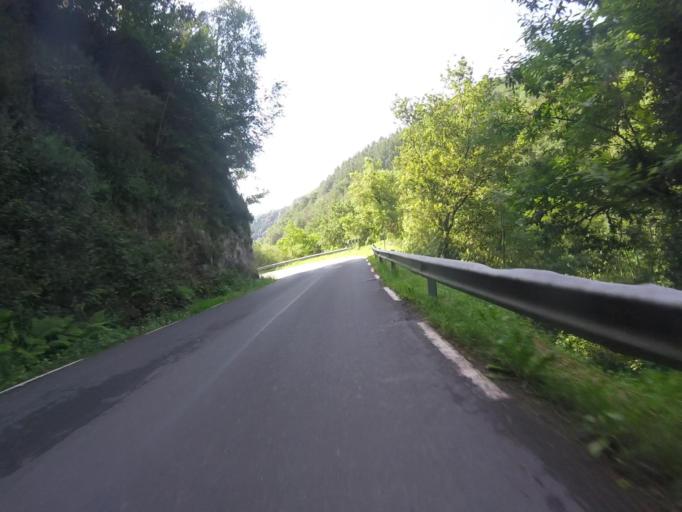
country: ES
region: Basque Country
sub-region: Provincia de Guipuzcoa
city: Hernialde
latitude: 43.1651
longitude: -2.0920
